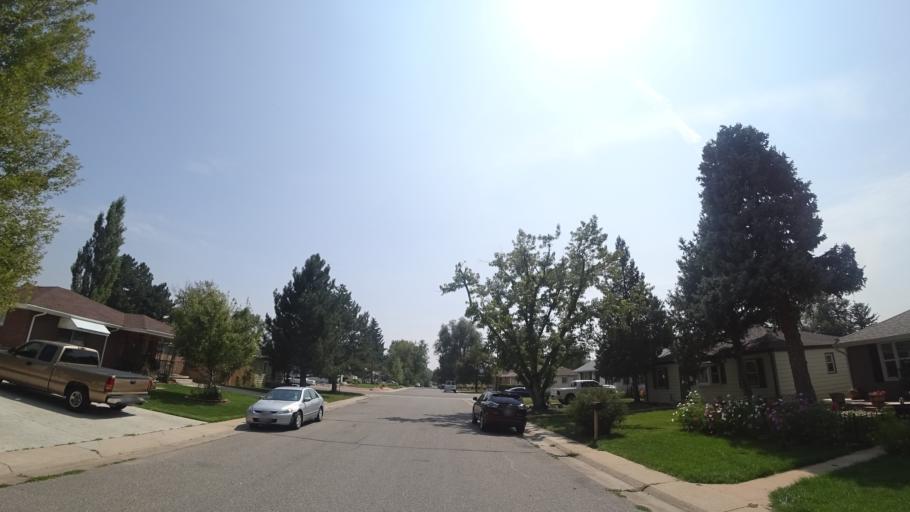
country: US
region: Colorado
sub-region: Arapahoe County
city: Englewood
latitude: 39.6373
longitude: -104.9937
